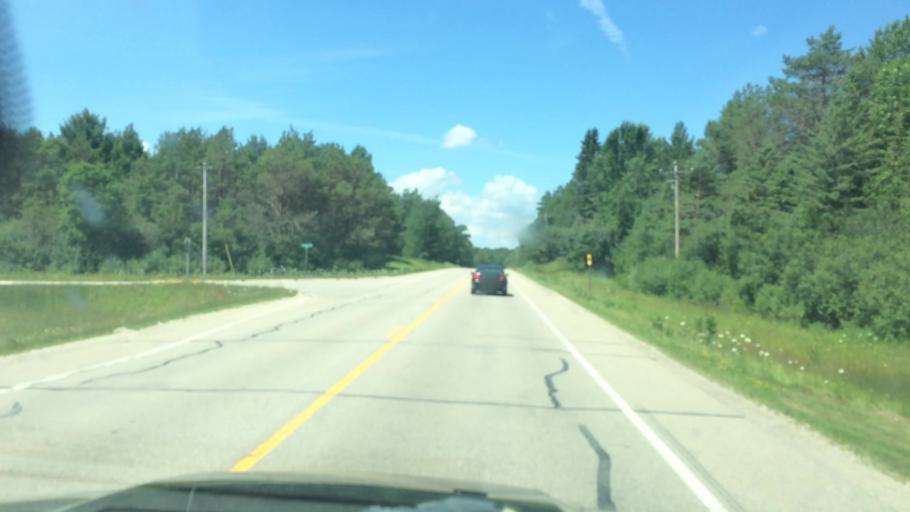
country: US
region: Wisconsin
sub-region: Marinette County
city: Peshtigo
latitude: 45.1003
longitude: -87.7329
